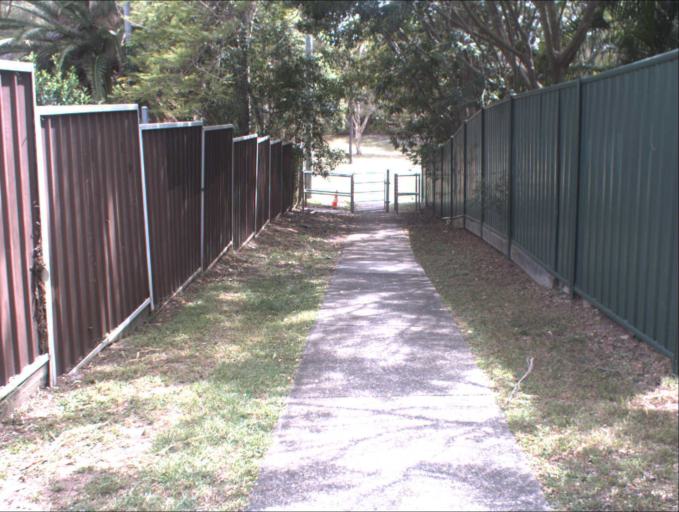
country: AU
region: Queensland
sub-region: Logan
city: Beenleigh
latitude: -27.7196
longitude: 153.1853
